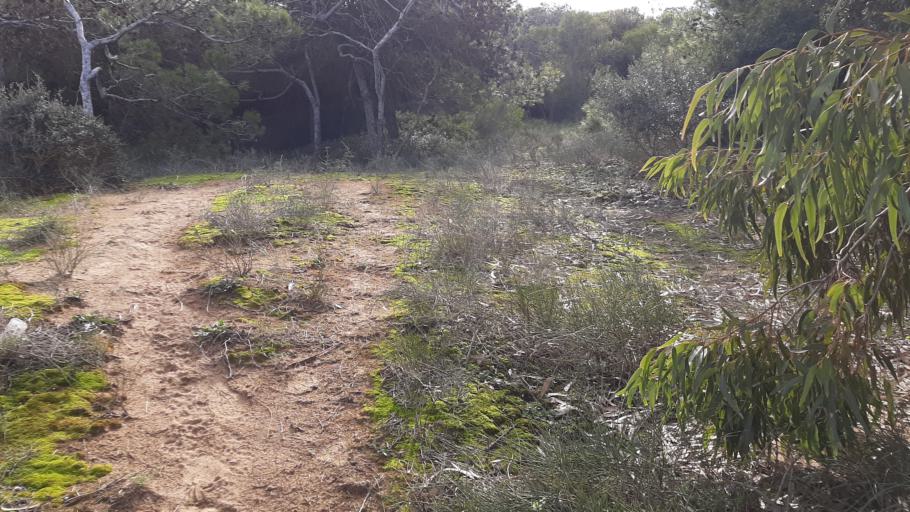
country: TN
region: Tunis
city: Al Marsa
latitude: 36.9188
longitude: 10.3029
